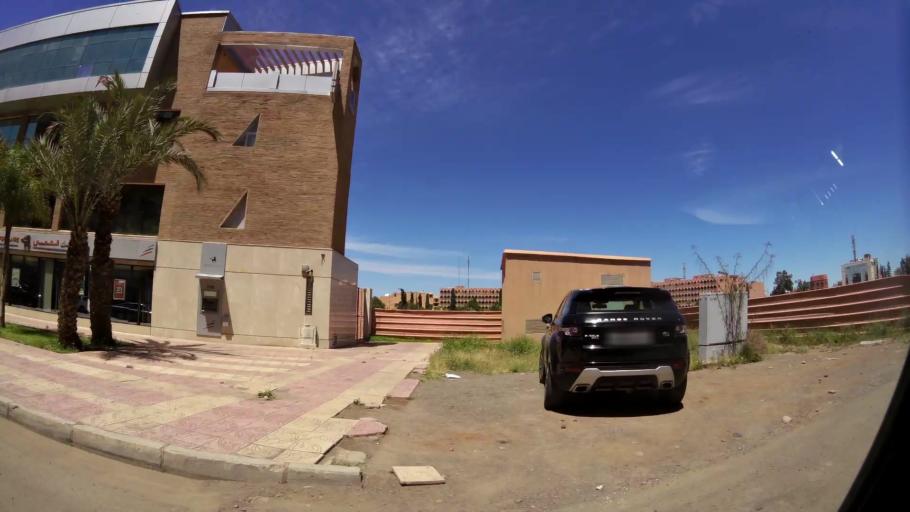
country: MA
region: Marrakech-Tensift-Al Haouz
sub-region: Marrakech
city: Marrakesh
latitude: 31.6207
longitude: -8.0124
